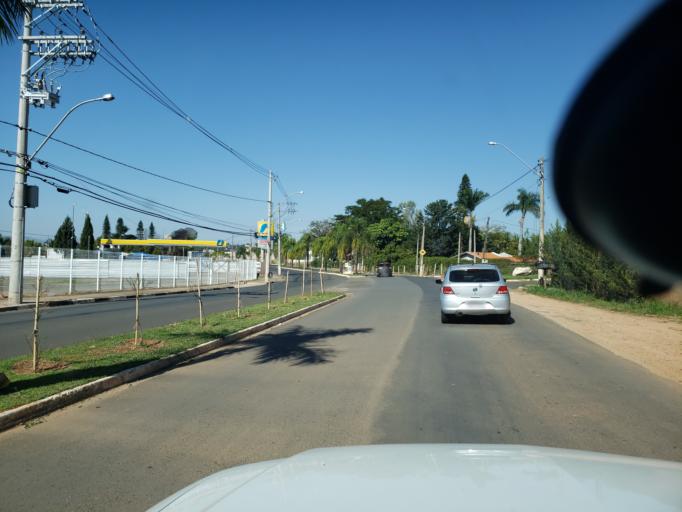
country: BR
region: Sao Paulo
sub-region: Itapira
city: Itapira
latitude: -22.4202
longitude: -46.8389
